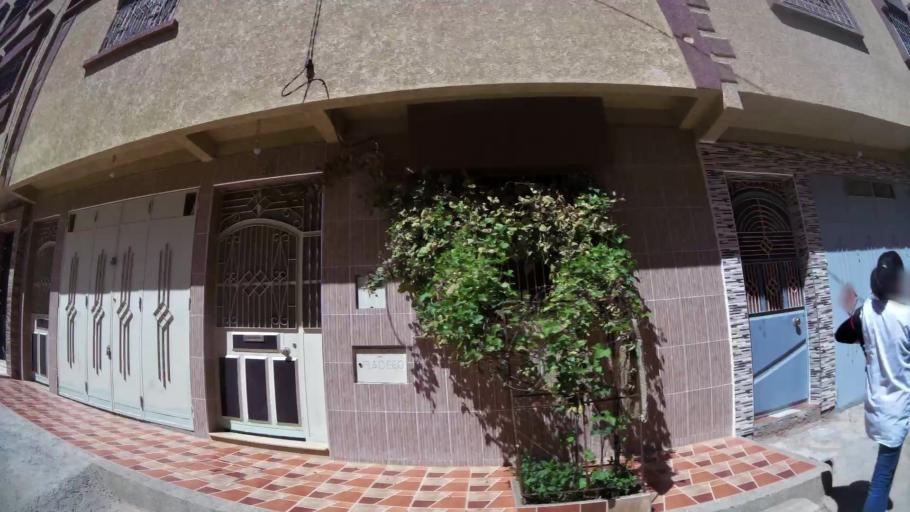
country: MA
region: Oriental
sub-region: Oujda-Angad
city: Oujda
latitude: 34.6578
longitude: -1.8761
